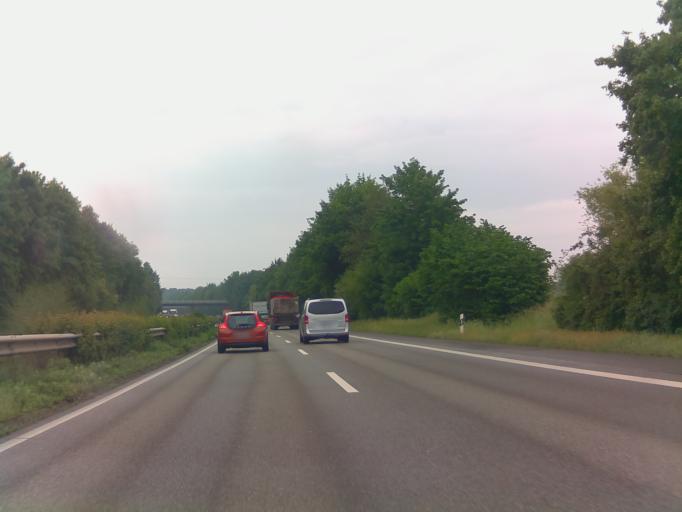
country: DE
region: Rheinland-Pfalz
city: Lingenfeld
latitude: 49.2537
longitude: 8.3315
